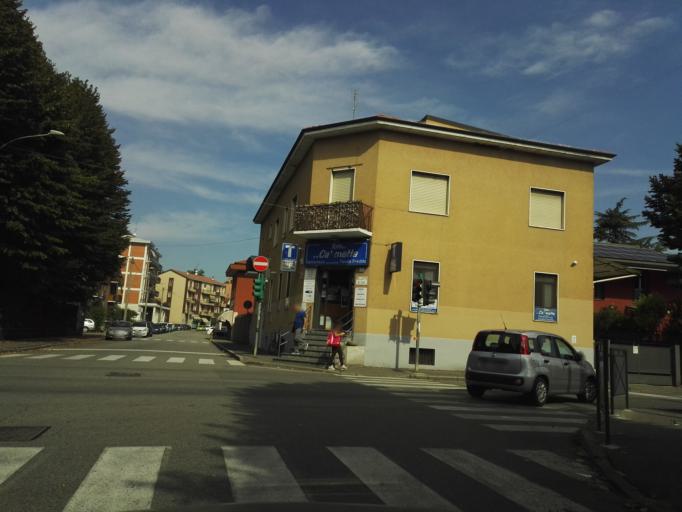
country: IT
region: Lombardy
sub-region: Citta metropolitana di Milano
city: Bettola-Zeloforomagno
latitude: 45.4295
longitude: 9.3115
